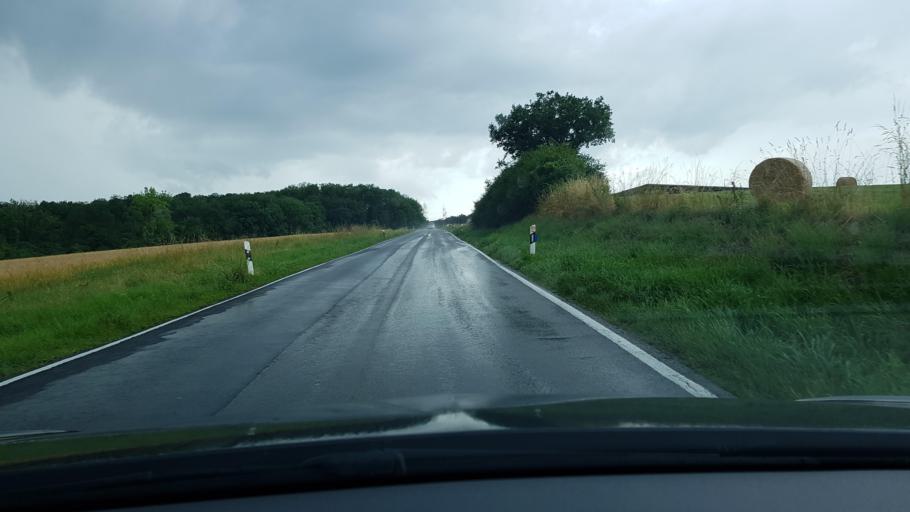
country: DE
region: Rheinland-Pfalz
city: Sinzig
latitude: 50.5162
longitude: 7.2381
